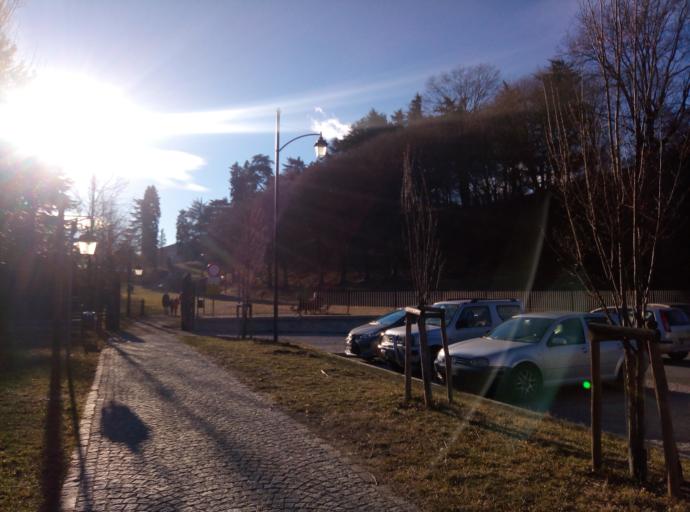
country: IT
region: Piedmont
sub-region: Provincia di Torino
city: Rivoli
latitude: 45.0680
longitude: 7.5068
